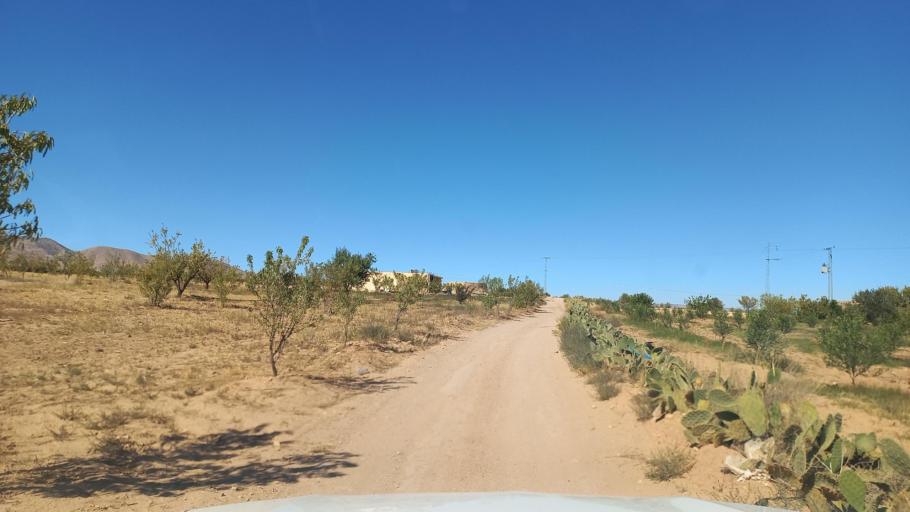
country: TN
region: Al Qasrayn
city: Sbiba
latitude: 35.3975
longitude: 9.0840
